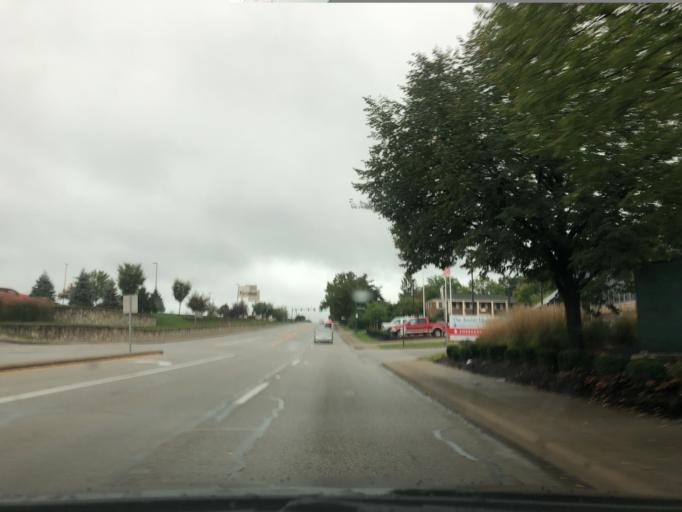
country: US
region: Ohio
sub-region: Hamilton County
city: Rossmoyne
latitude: 39.2058
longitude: -84.3798
